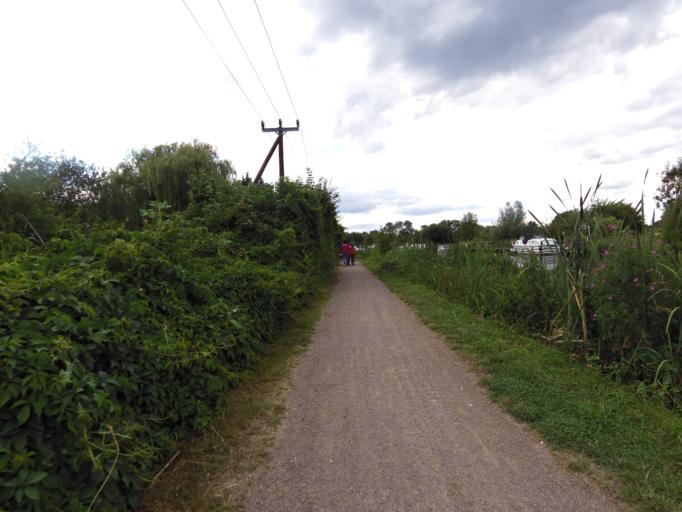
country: GB
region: England
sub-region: Hertfordshire
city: Broxbourne
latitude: 51.7340
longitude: -0.0132
